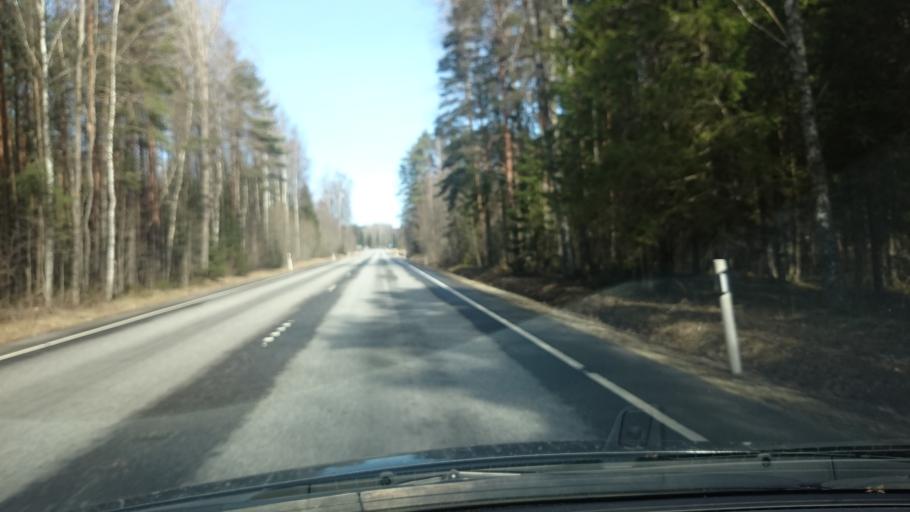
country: EE
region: Jaervamaa
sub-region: Tueri vald
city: Sarevere
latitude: 58.7117
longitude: 25.2695
